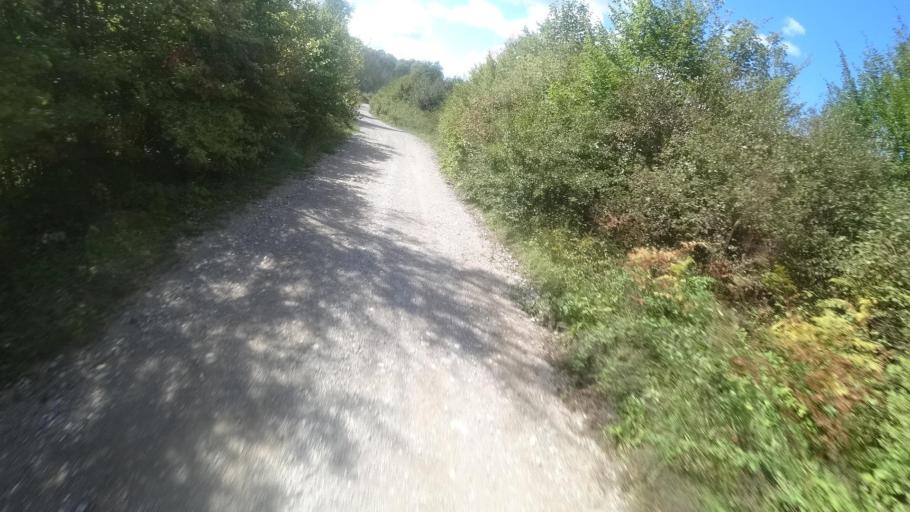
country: BA
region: Federation of Bosnia and Herzegovina
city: Ostrozac
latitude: 44.8347
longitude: 15.9915
